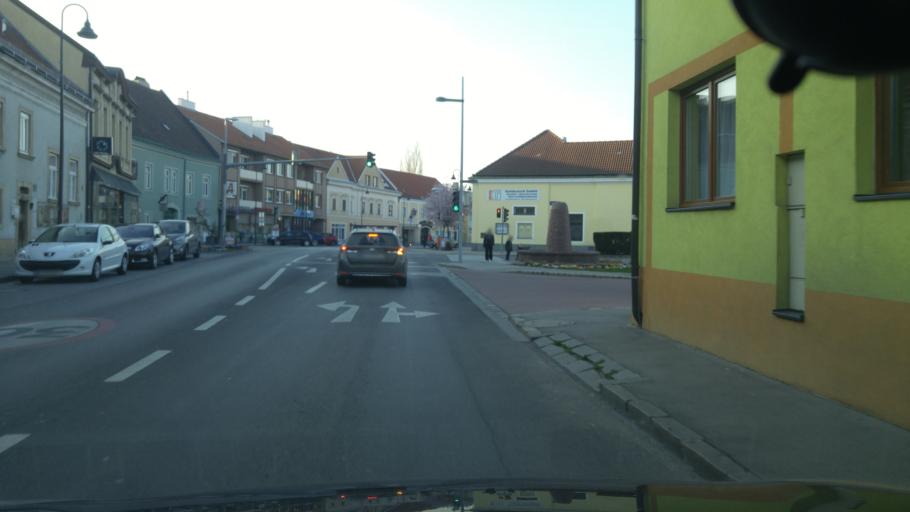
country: AT
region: Lower Austria
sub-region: Politischer Bezirk Wien-Umgebung
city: Himberg
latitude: 48.0818
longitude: 16.4397
